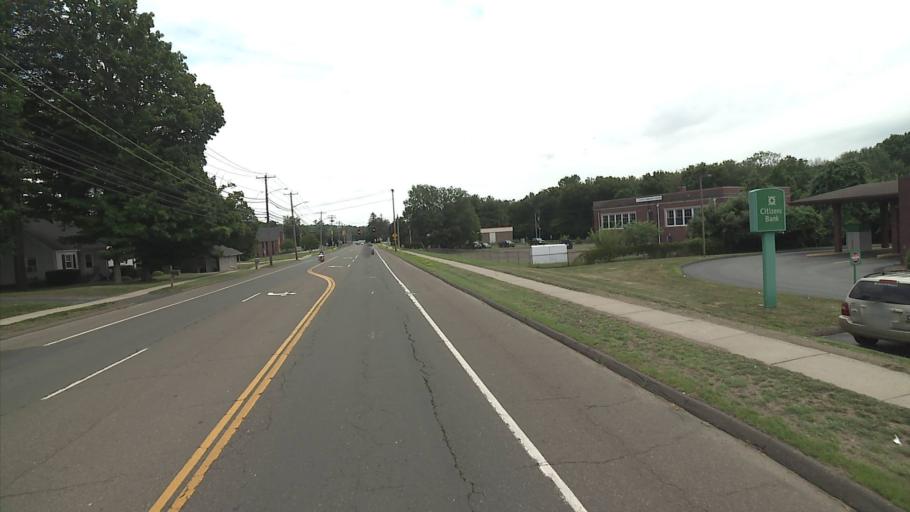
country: US
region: Connecticut
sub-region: New Haven County
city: Branford
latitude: 41.3240
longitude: -72.8413
